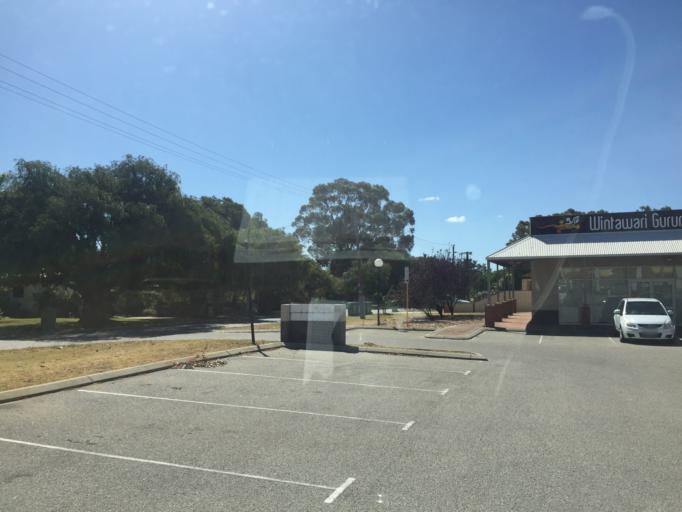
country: AU
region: Western Australia
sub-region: Belmont
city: Redcliffe
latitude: -31.9292
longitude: 115.9451
